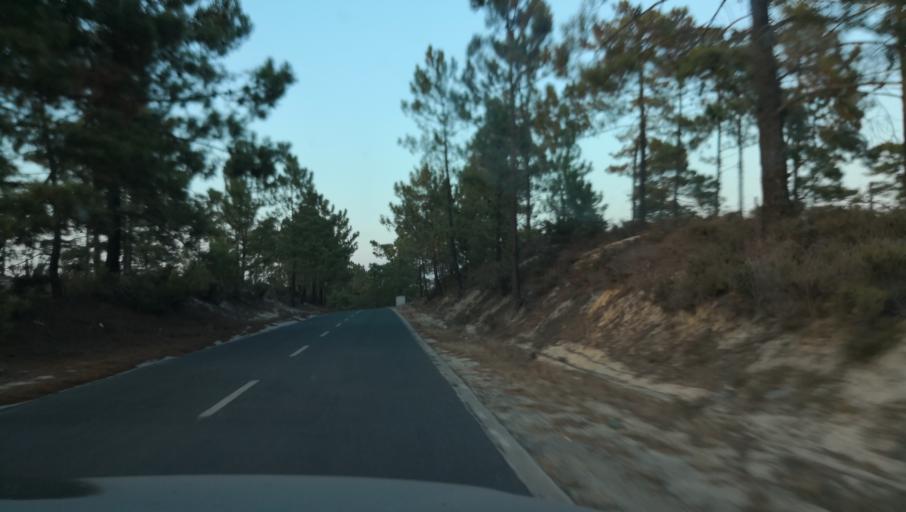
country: PT
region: Setubal
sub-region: Setubal
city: Setubal
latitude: 38.3892
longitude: -8.7809
